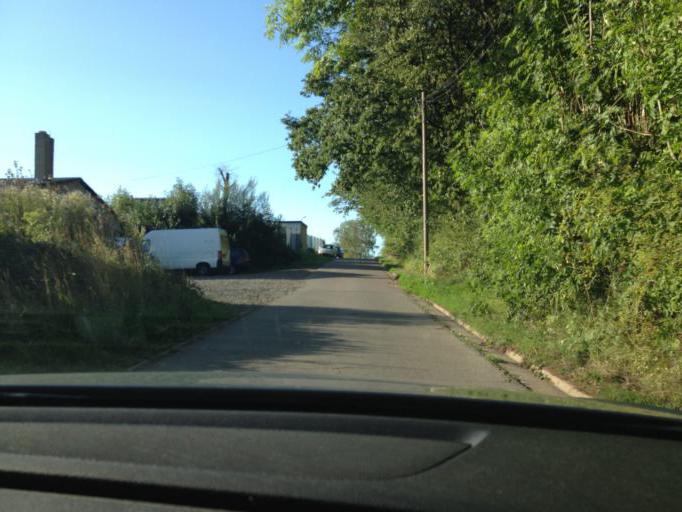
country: DE
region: Saarland
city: Tholey
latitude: 49.5020
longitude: 7.0139
